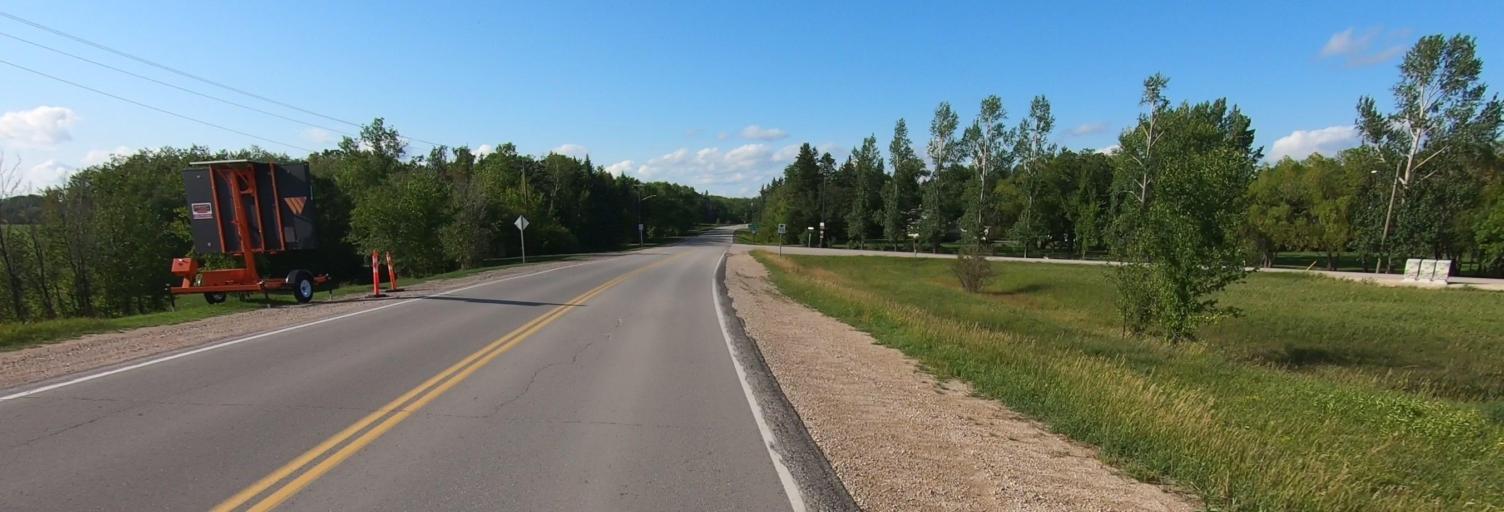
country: CA
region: Manitoba
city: Selkirk
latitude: 50.0931
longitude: -96.9317
